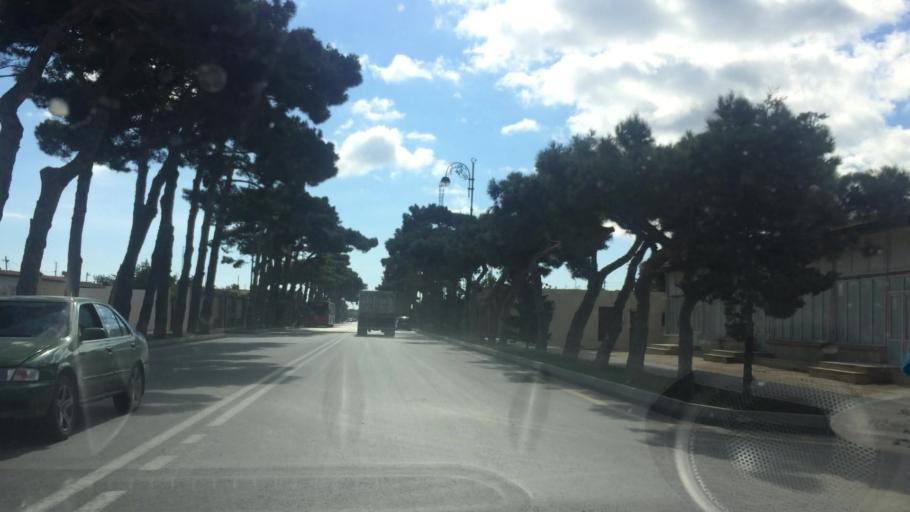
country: AZ
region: Baki
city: Pirallahi
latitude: 40.4655
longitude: 50.3279
